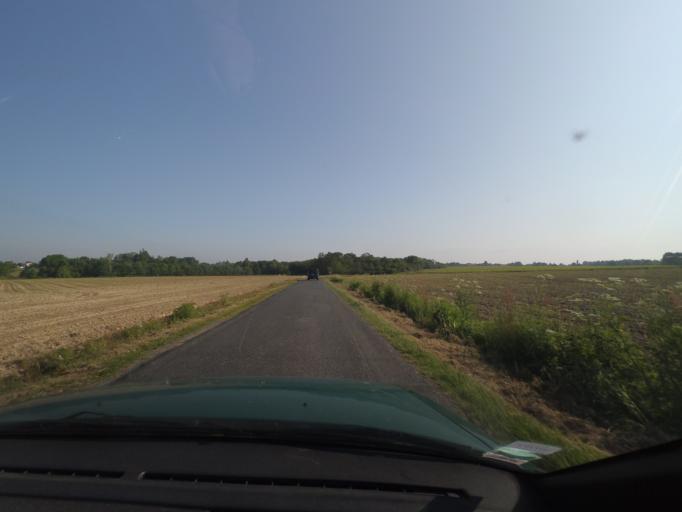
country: FR
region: Pays de la Loire
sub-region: Departement de la Loire-Atlantique
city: Maisdon-sur-Sevre
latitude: 47.0896
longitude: -1.3709
